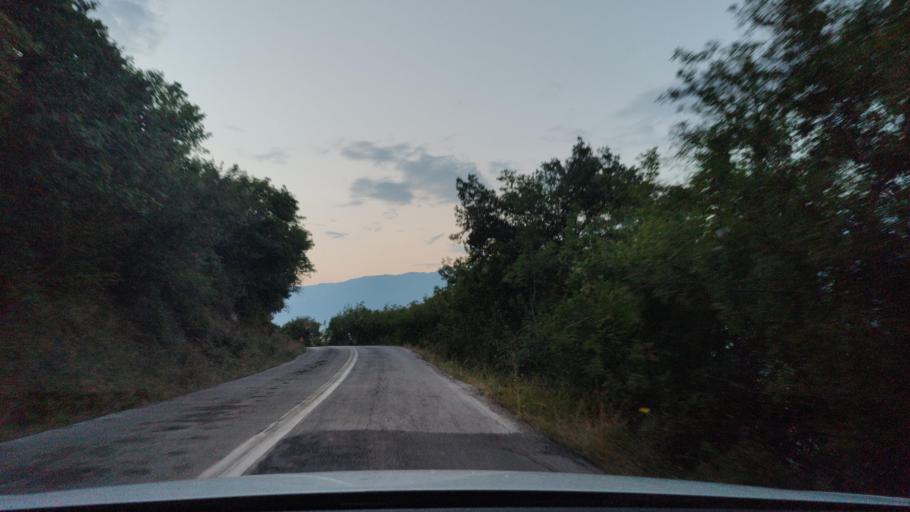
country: GR
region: Central Macedonia
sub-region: Nomos Serron
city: Chrysochorafa
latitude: 41.1713
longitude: 23.1751
